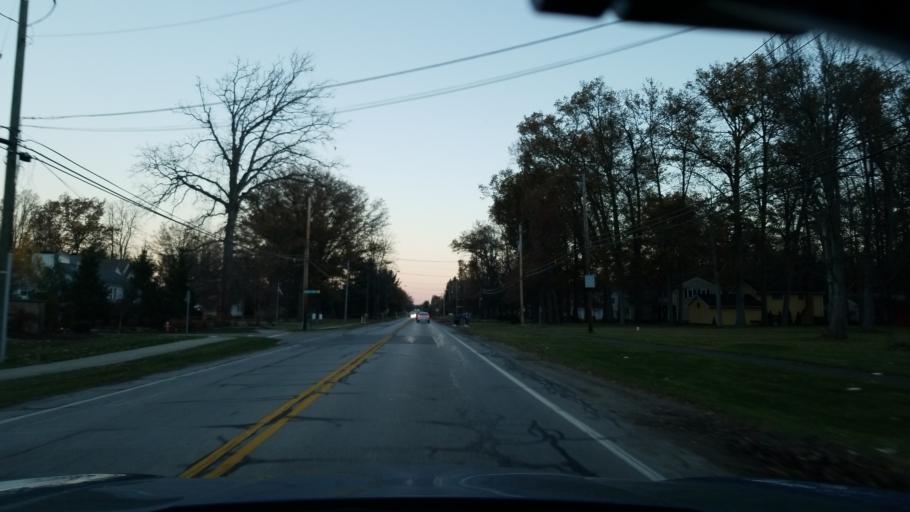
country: US
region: Ohio
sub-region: Cuyahoga County
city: Berea
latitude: 41.3383
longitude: -81.8576
